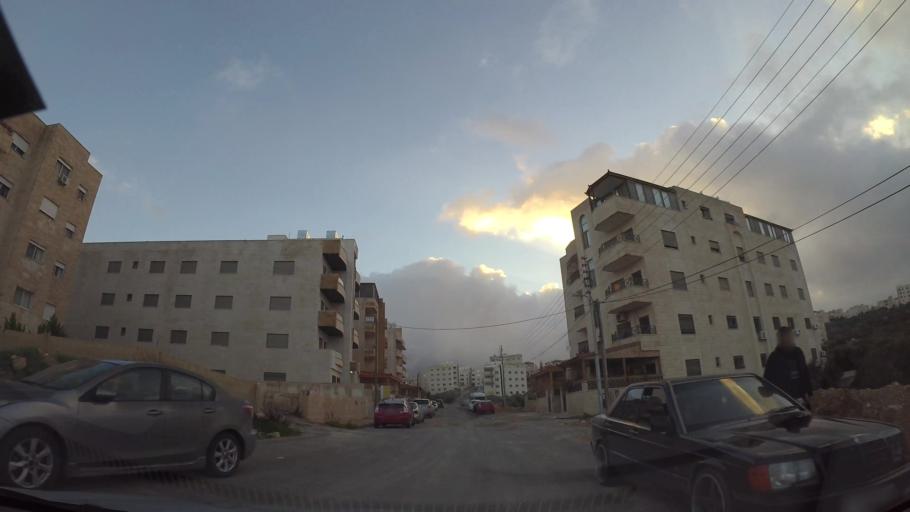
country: JO
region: Amman
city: Al Jubayhah
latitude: 32.0495
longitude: 35.9030
